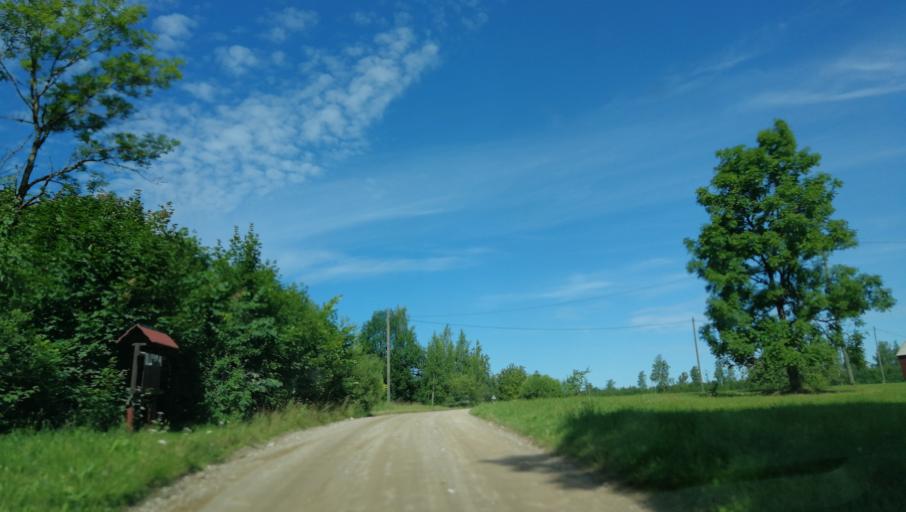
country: LV
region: Gulbenes Rajons
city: Gulbene
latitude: 57.1762
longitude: 26.8743
